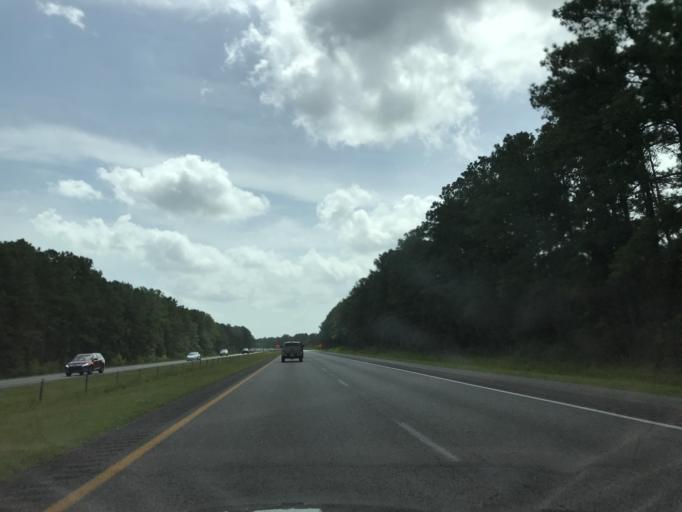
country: US
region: North Carolina
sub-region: New Hanover County
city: Castle Hayne
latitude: 34.3781
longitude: -77.8830
